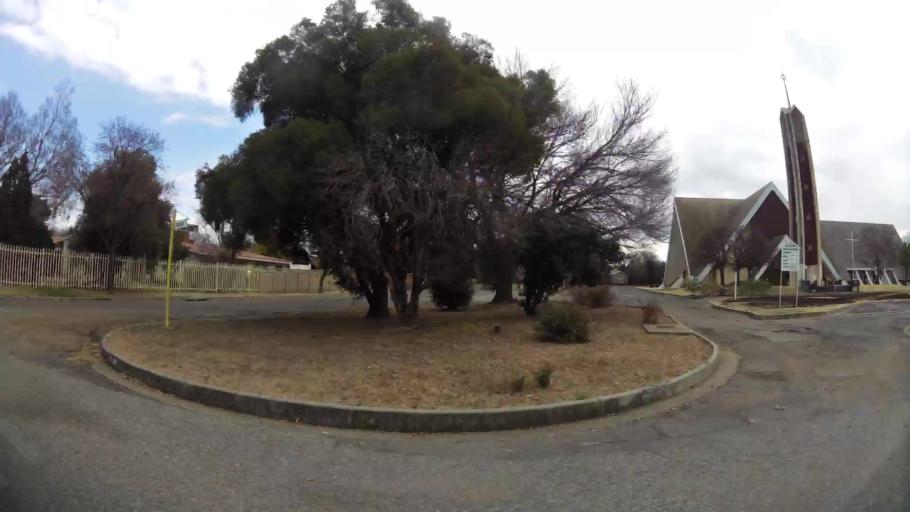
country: ZA
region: Orange Free State
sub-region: Fezile Dabi District Municipality
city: Kroonstad
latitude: -27.6411
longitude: 27.2374
